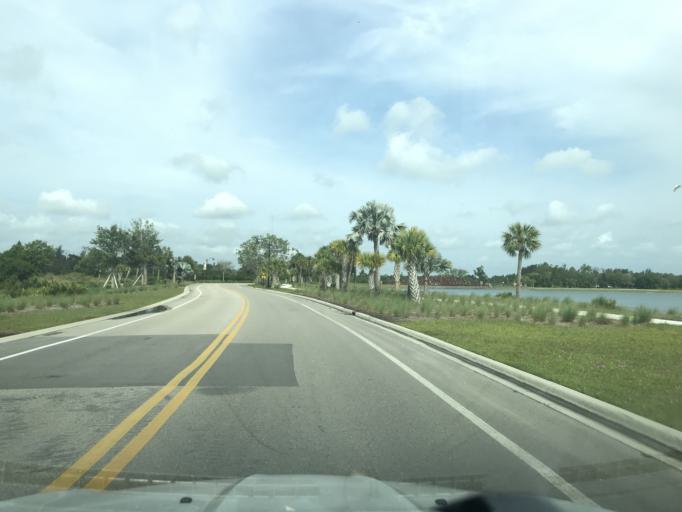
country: US
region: Florida
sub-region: Lee County
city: Fort Myers Shores
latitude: 26.7848
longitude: -81.7562
